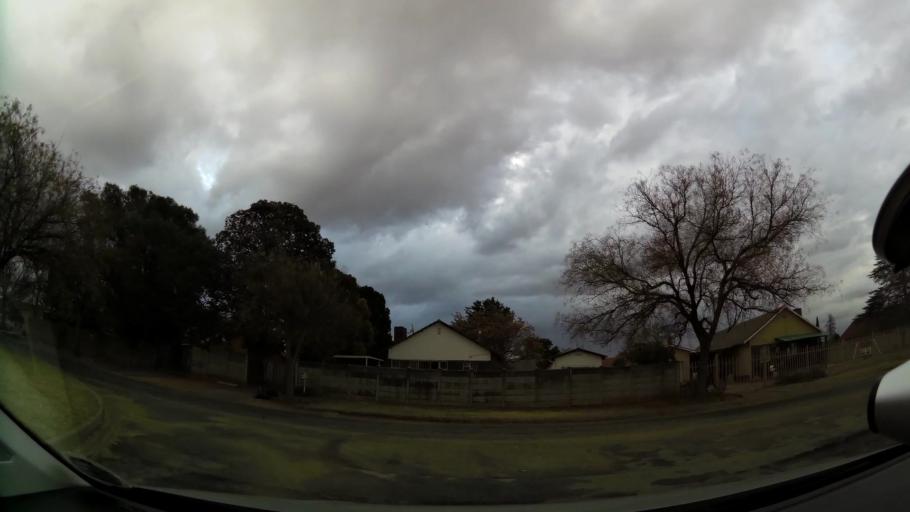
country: ZA
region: Orange Free State
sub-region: Lejweleputswa District Municipality
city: Welkom
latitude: -27.9661
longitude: 26.7216
